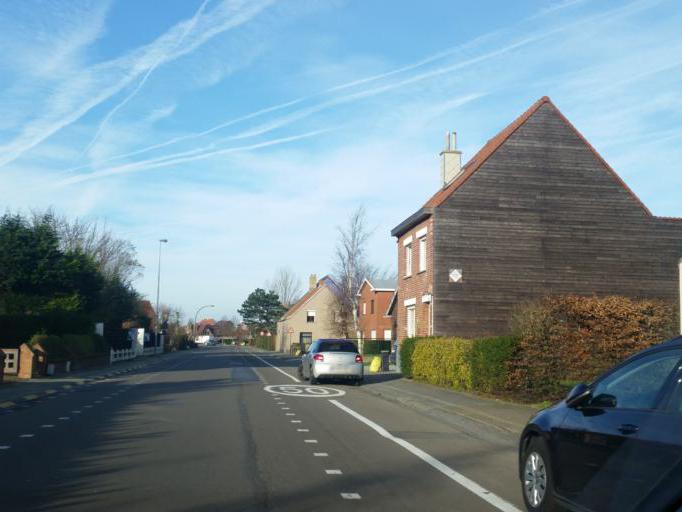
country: BE
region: Flanders
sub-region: Provincie West-Vlaanderen
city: De Haan
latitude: 51.2697
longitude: 3.0489
